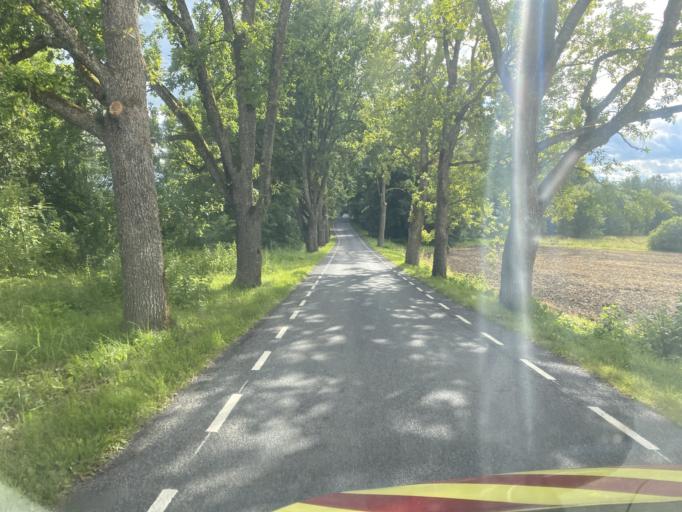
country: EE
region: Viljandimaa
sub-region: Viljandi linn
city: Viljandi
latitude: 58.3956
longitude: 25.6066
